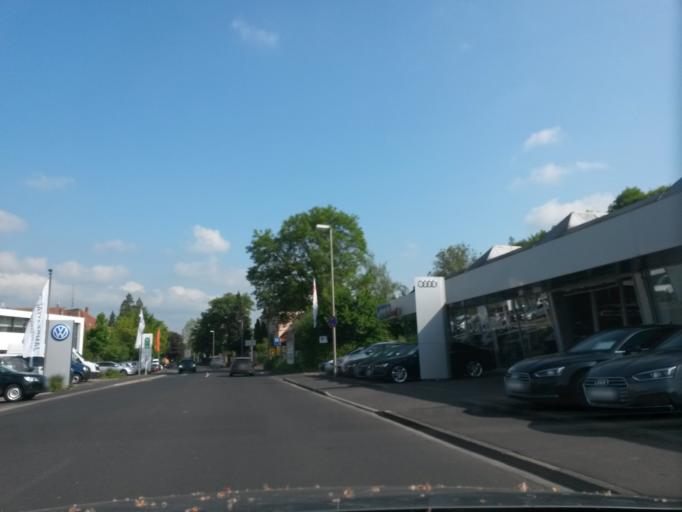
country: DE
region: Bavaria
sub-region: Regierungsbezirk Unterfranken
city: Bad Kissingen
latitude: 50.1856
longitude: 10.0777
